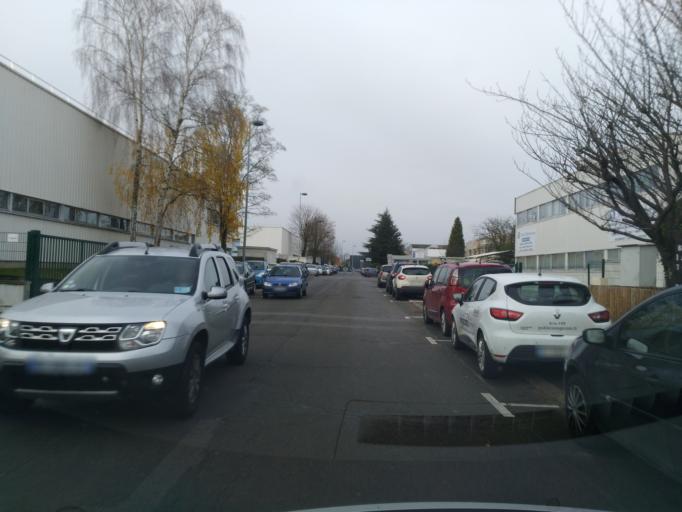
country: FR
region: Ile-de-France
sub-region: Departement des Yvelines
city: Les Clayes-sous-Bois
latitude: 48.8269
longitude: 1.9749
